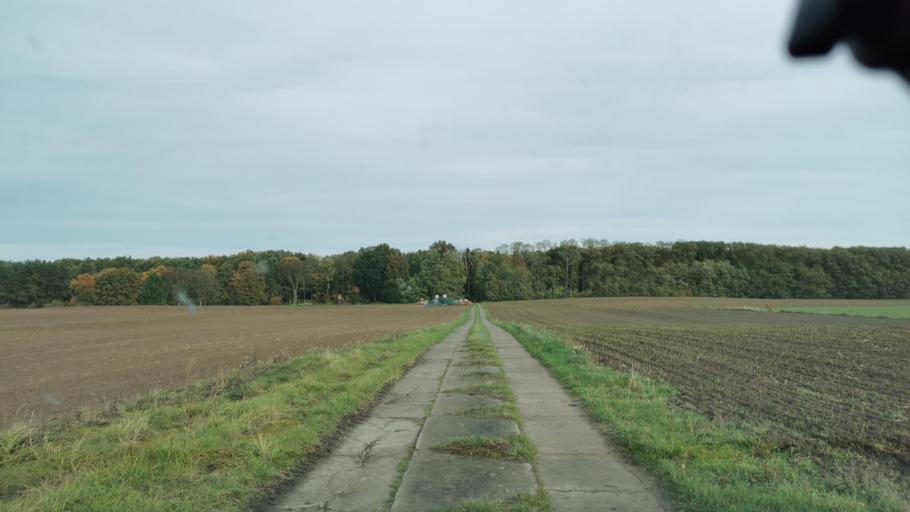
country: DE
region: Brandenburg
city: Eberswalde
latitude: 52.7809
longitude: 13.8562
